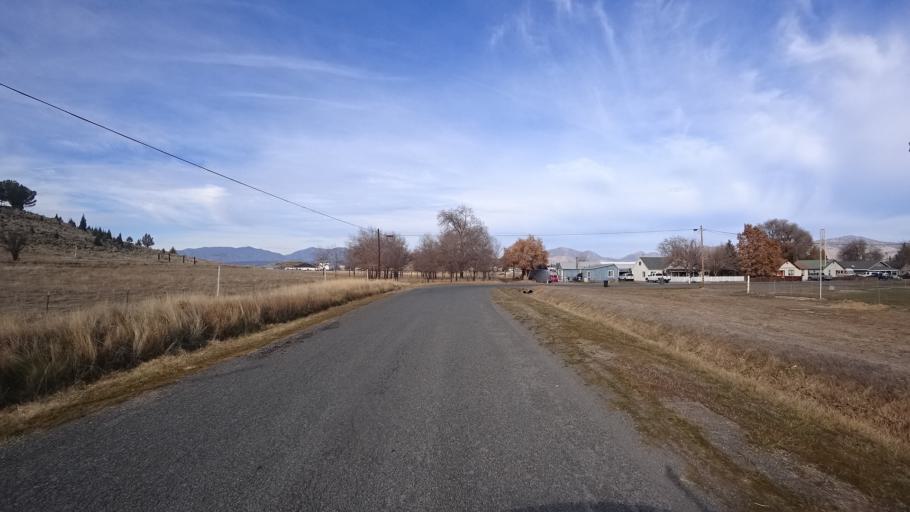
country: US
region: California
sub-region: Siskiyou County
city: Montague
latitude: 41.7220
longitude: -122.5272
